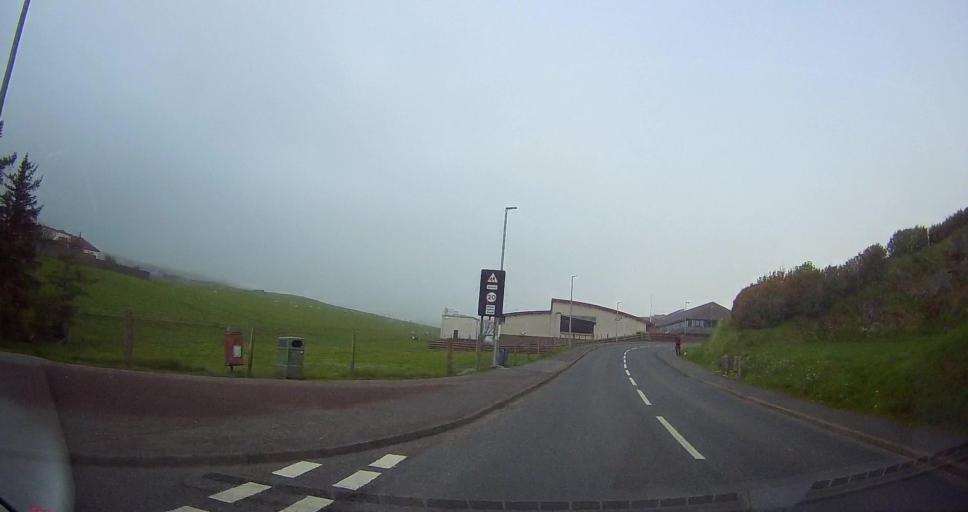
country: GB
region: Scotland
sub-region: Shetland Islands
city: Lerwick
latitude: 60.1388
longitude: -1.2741
